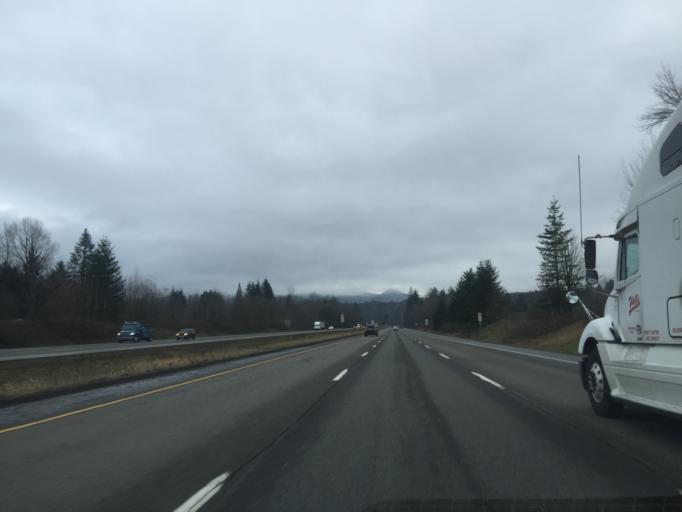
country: US
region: Washington
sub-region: King County
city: North Bend
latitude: 47.4840
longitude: -121.7924
